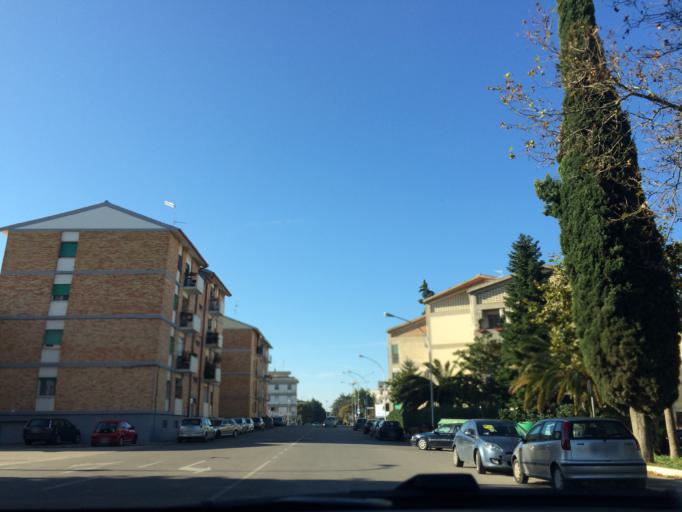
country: IT
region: Basilicate
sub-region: Provincia di Matera
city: Matera
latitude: 40.6776
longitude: 16.5916
